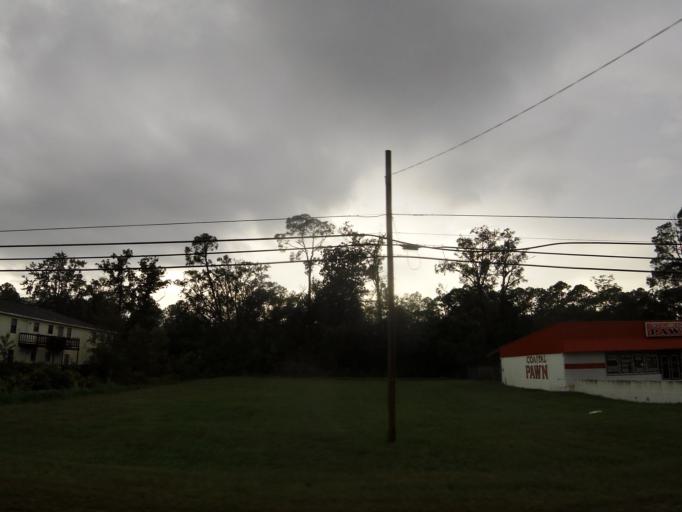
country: US
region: Georgia
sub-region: Wayne County
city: Jesup
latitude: 31.5979
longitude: -81.8741
